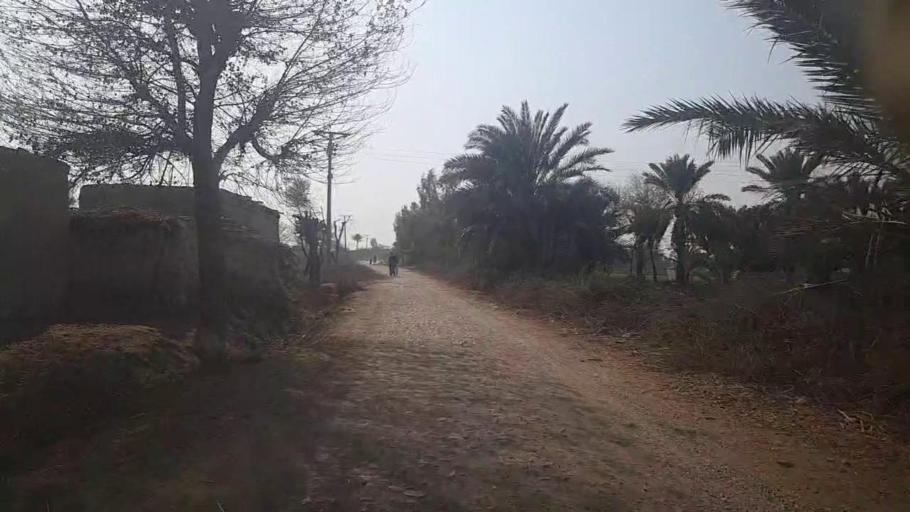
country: PK
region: Sindh
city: Kot Diji
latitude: 27.3612
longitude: 68.7427
